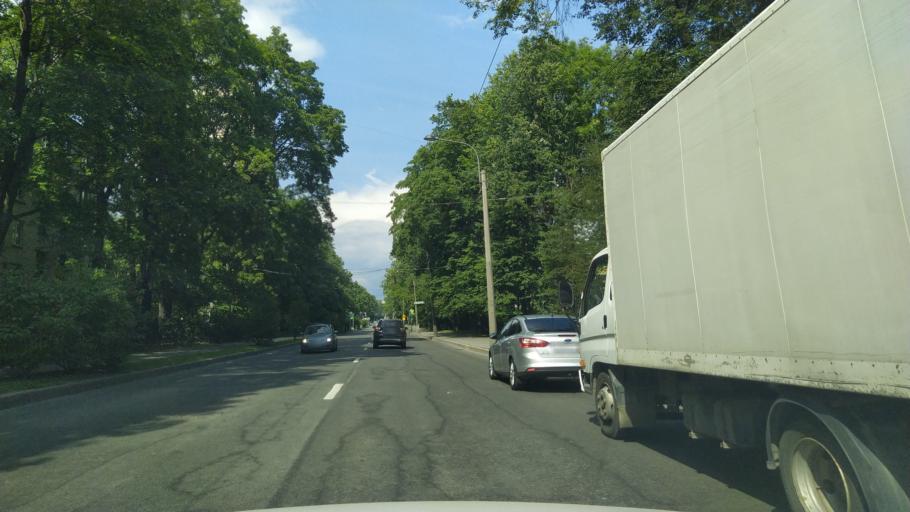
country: RU
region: Leningrad
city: Sampsonievskiy
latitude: 59.9972
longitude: 30.3460
